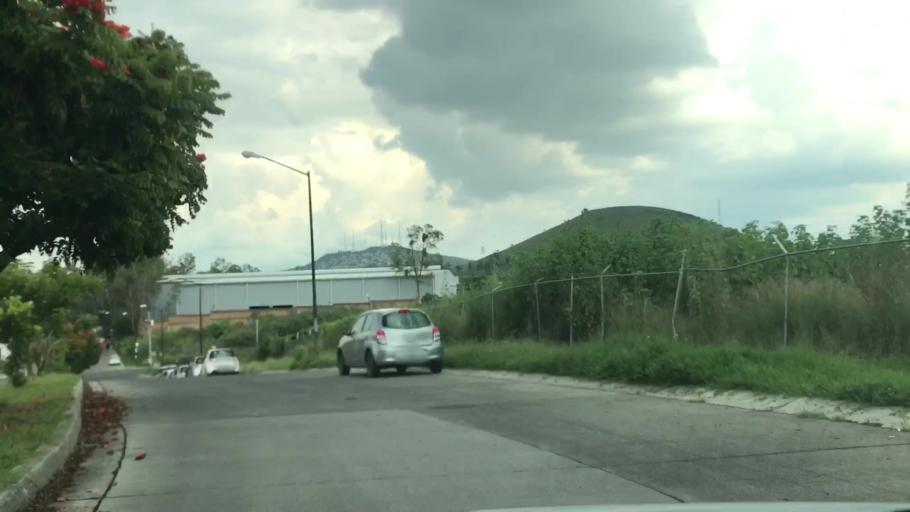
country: MX
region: Jalisco
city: Guadalajara
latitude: 20.6172
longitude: -103.3979
